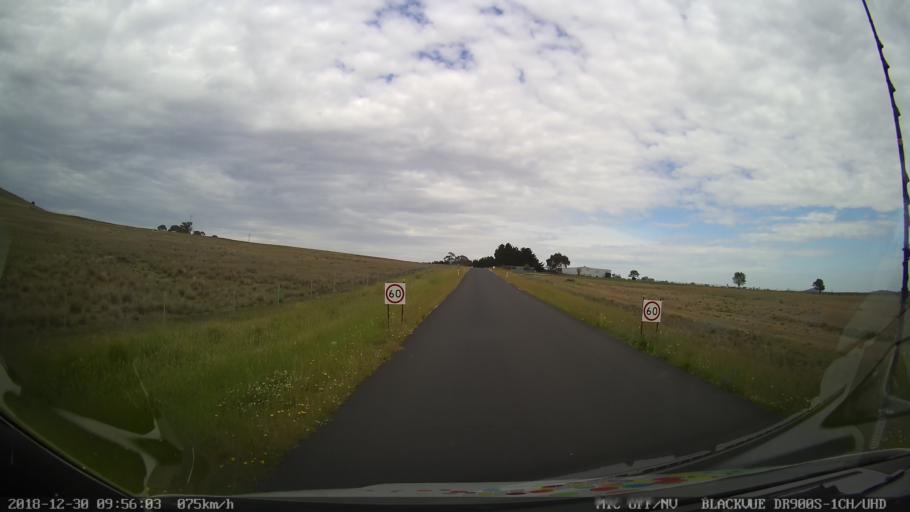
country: AU
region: New South Wales
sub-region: Cooma-Monaro
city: Cooma
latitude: -36.5221
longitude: 149.2562
